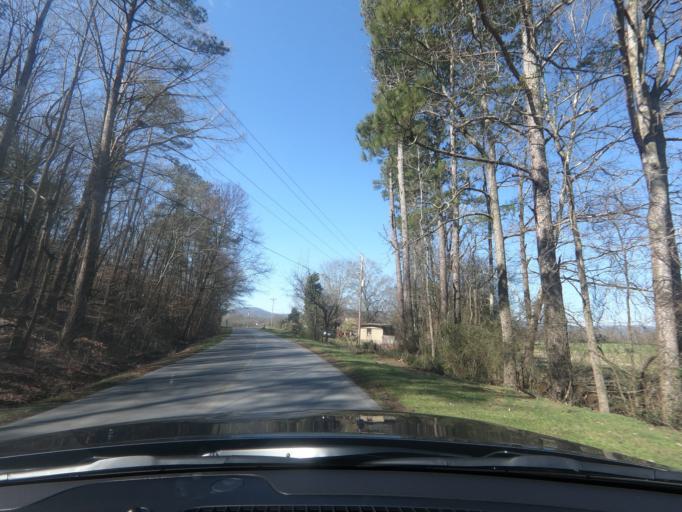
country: US
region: Georgia
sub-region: Gordon County
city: Calhoun
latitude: 34.4625
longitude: -85.0004
